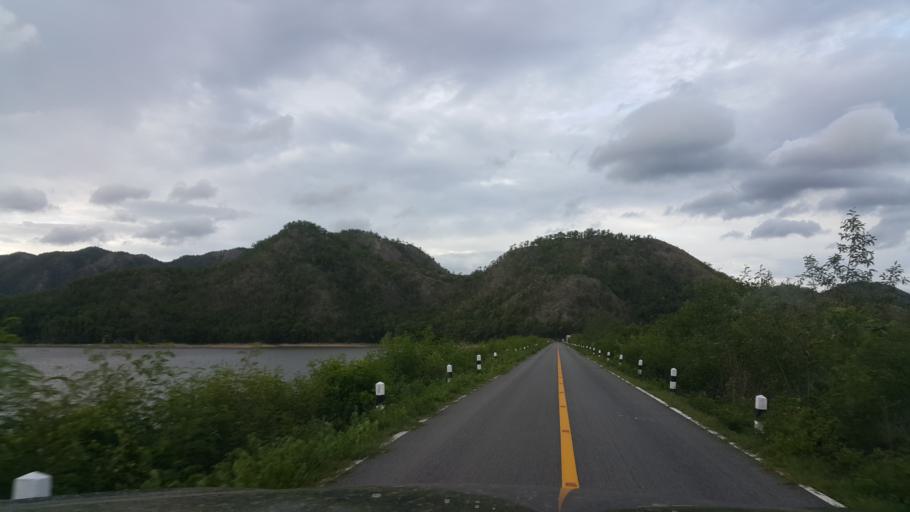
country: TH
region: Sukhothai
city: Thung Saliam
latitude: 17.1765
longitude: 99.4811
